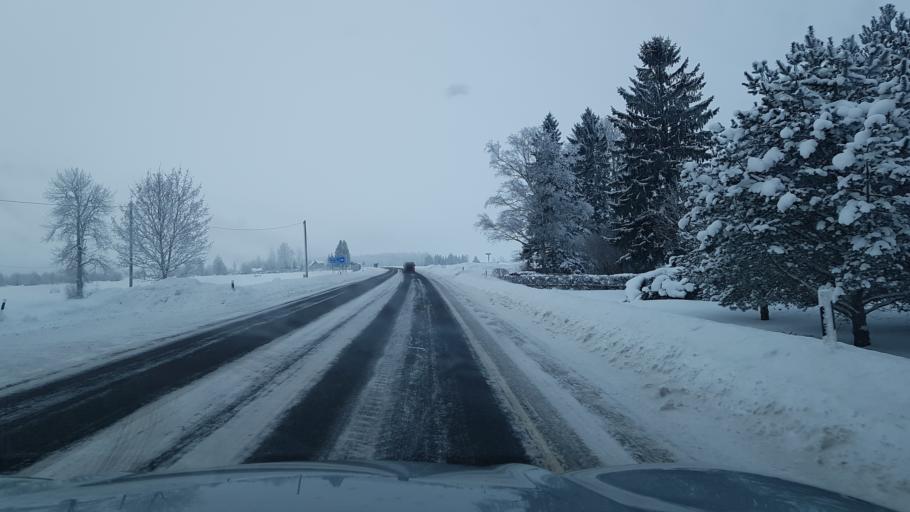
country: EE
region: Ida-Virumaa
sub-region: Johvi vald
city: Johvi
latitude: 59.2727
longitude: 27.3868
